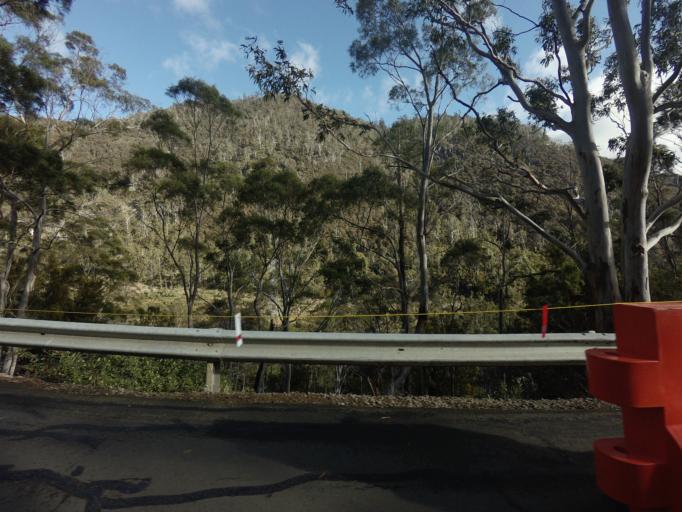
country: AU
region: Tasmania
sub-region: Glenorchy
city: Berriedale
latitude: -42.8187
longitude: 147.1791
